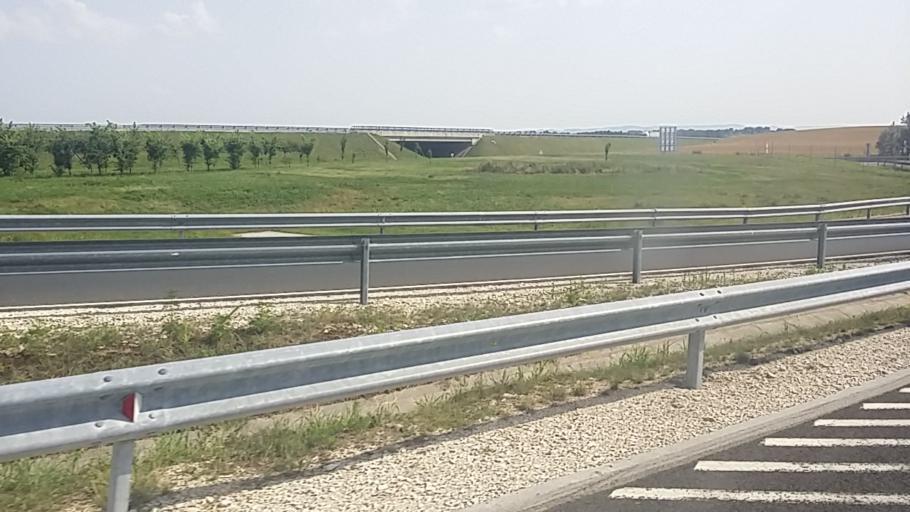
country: HU
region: Tolna
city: Szedres
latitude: 46.4708
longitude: 18.7162
